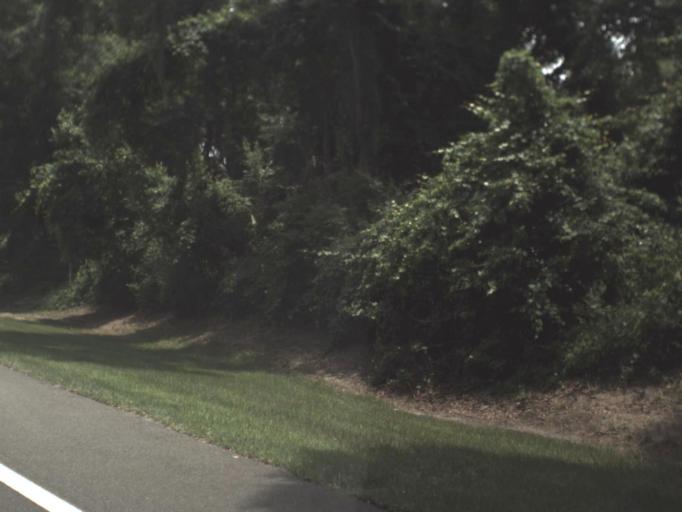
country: US
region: Florida
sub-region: Nassau County
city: Fernandina Beach
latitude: 30.5638
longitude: -81.4529
